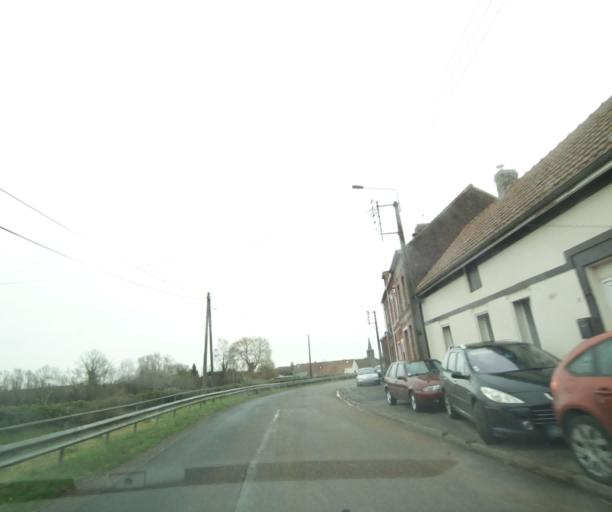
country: FR
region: Nord-Pas-de-Calais
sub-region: Departement du Nord
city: Crespin
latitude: 50.4414
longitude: 3.6311
